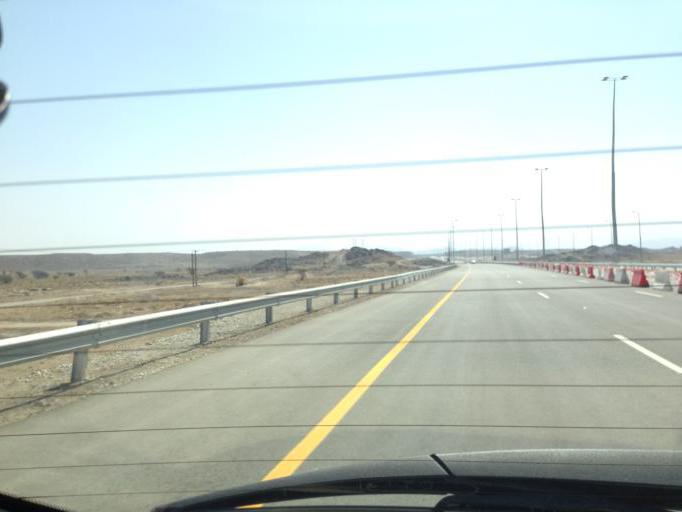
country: OM
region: Al Batinah
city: Rustaq
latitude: 23.5553
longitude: 57.5028
